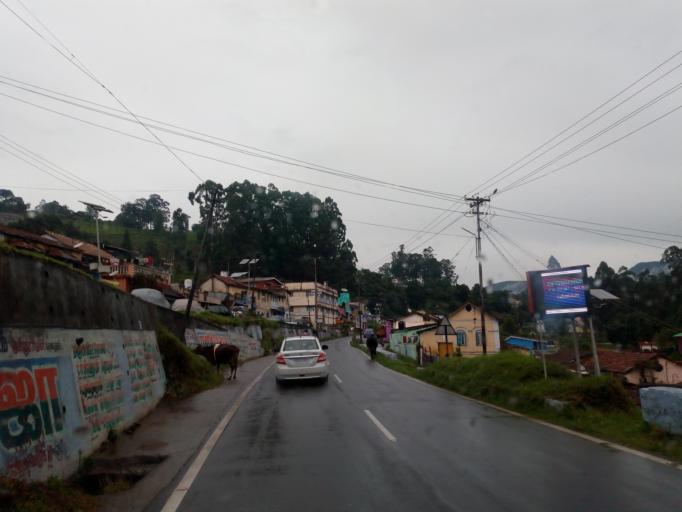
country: IN
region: Tamil Nadu
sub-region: Nilgiri
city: Wellington
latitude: 11.3541
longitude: 76.7855
